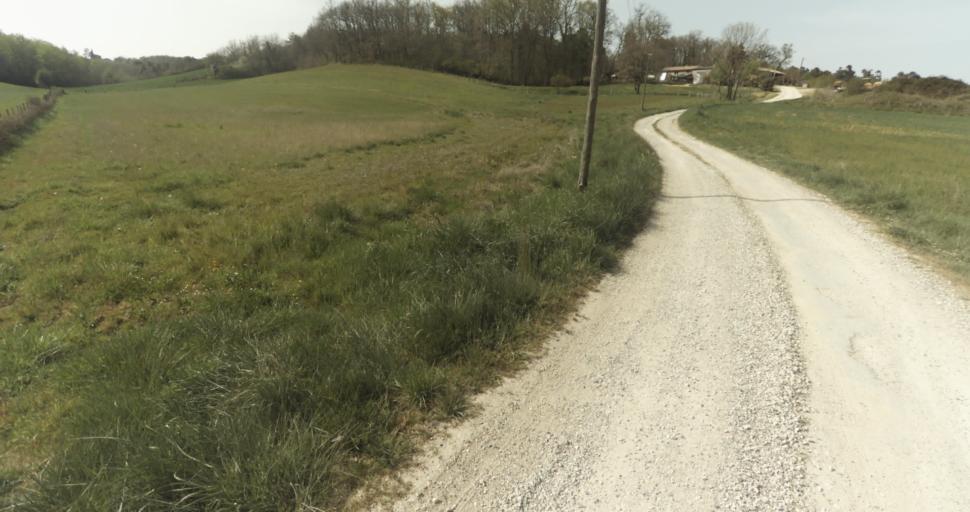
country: FR
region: Midi-Pyrenees
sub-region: Departement du Tarn-et-Garonne
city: Moissac
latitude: 44.1479
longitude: 1.1566
